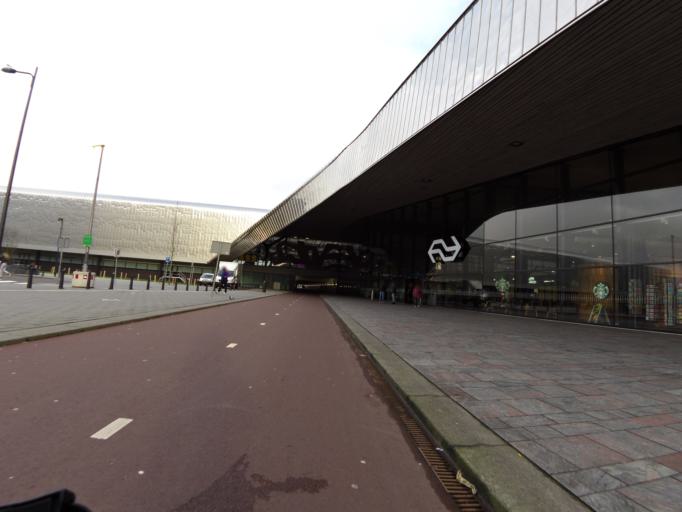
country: NL
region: South Holland
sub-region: Gemeente Rotterdam
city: Rotterdam
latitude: 51.9238
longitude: 4.4692
